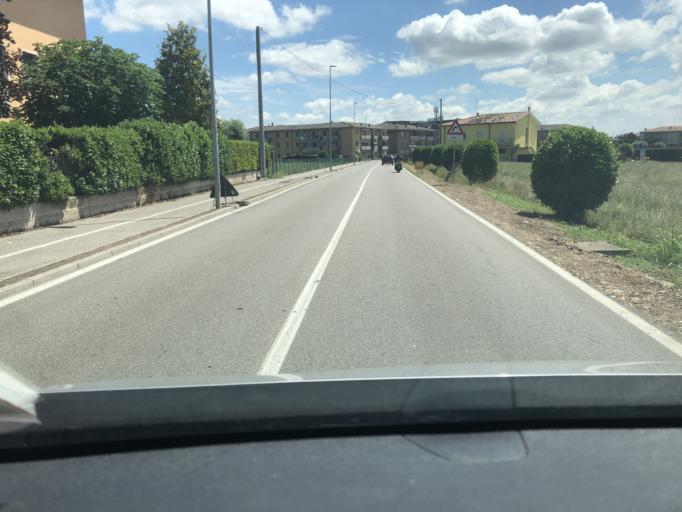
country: IT
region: Veneto
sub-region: Provincia di Verona
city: Villafranca di Verona
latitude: 45.3491
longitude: 10.8326
